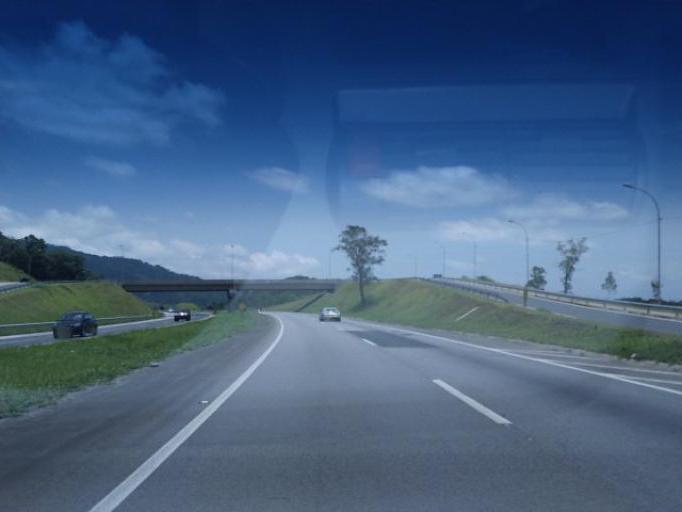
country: BR
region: Sao Paulo
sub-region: Miracatu
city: Miracatu
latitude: -24.2943
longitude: -47.4790
